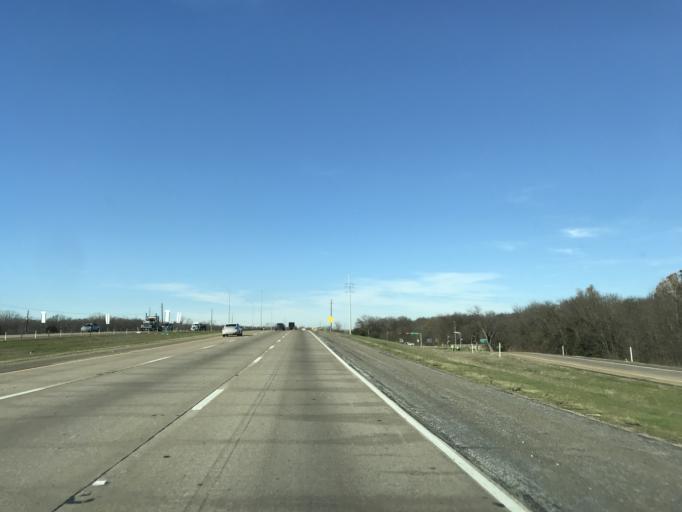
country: US
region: Texas
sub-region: Dallas County
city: Hutchins
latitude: 32.6800
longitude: -96.7425
